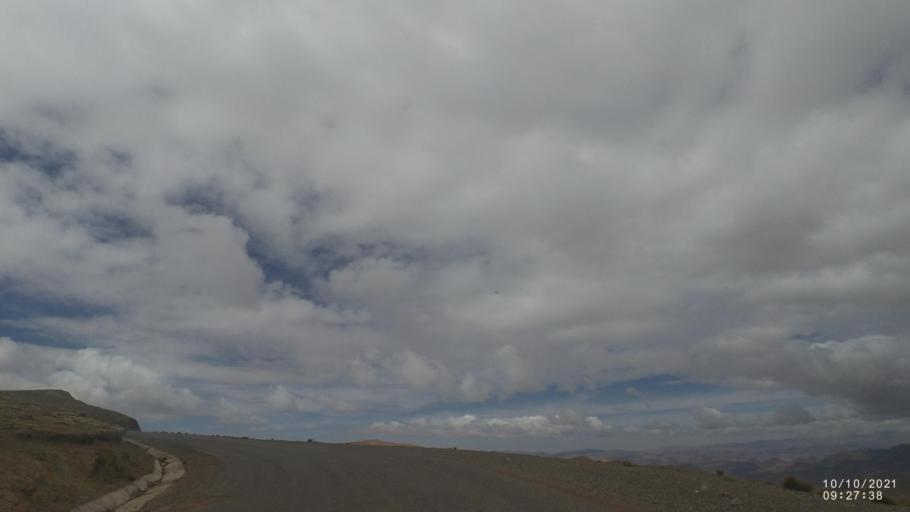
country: BO
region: La Paz
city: Quime
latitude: -17.1016
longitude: -67.3245
